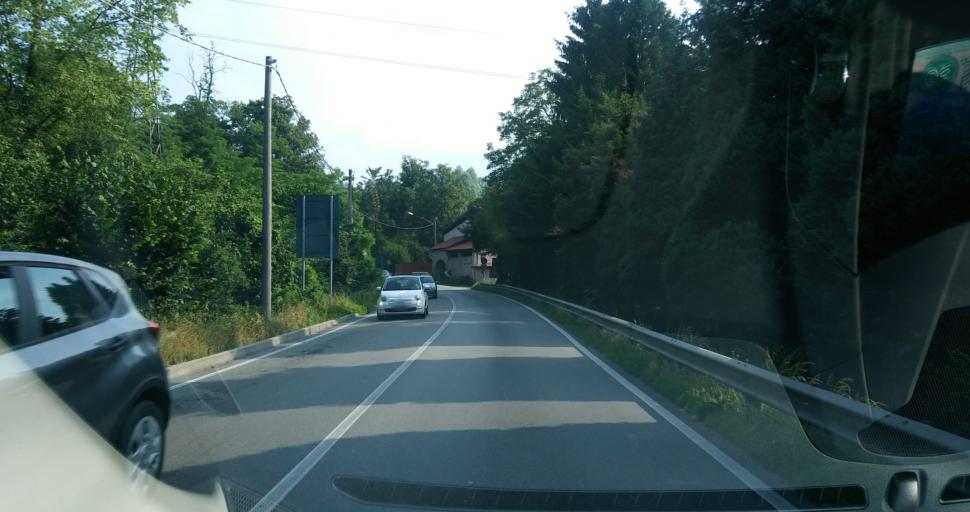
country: IT
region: Lombardy
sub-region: Provincia di Varese
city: Somma Lombardo
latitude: 45.6705
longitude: 8.7058
